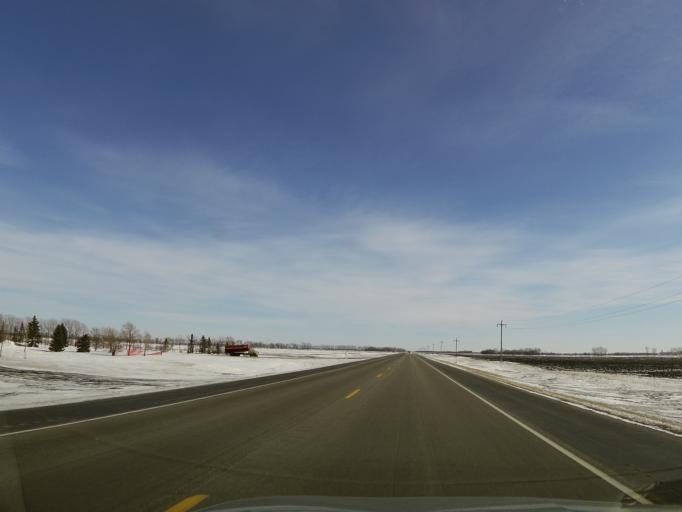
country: US
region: North Dakota
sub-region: Walsh County
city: Grafton
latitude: 48.4120
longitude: -97.2554
